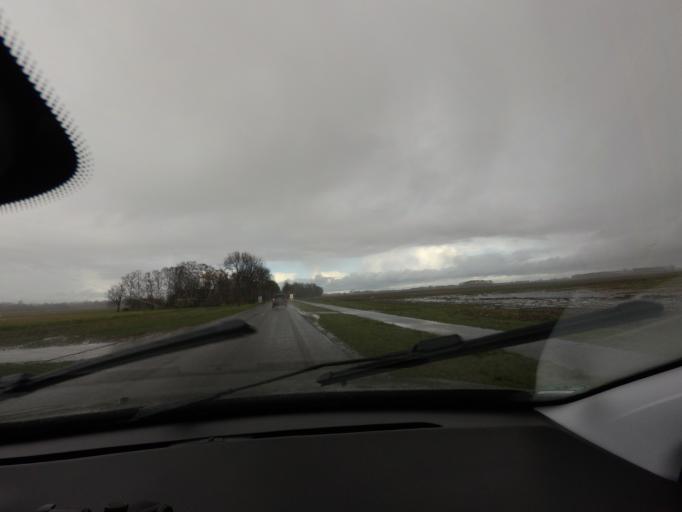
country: NL
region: Drenthe
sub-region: Gemeente Aa en Hunze
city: Anloo
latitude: 53.0218
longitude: 6.7888
